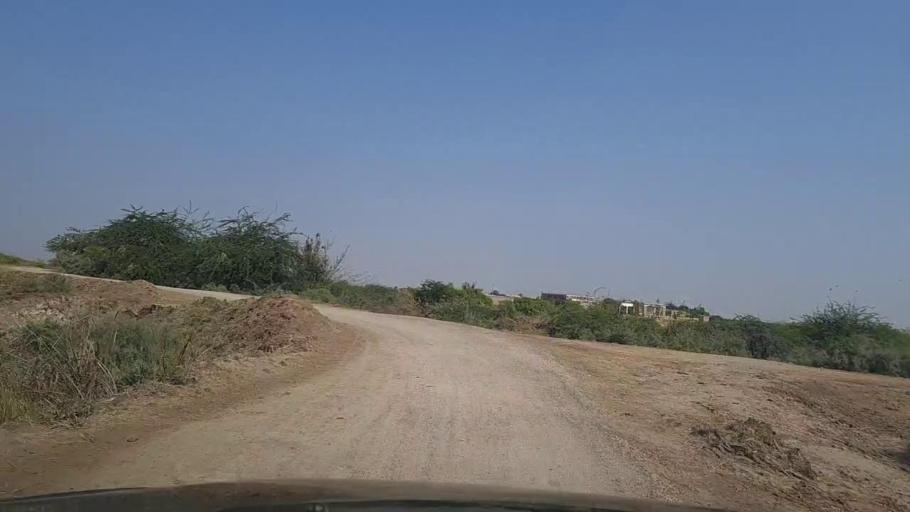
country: PK
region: Sindh
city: Thatta
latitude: 24.6469
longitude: 67.8170
